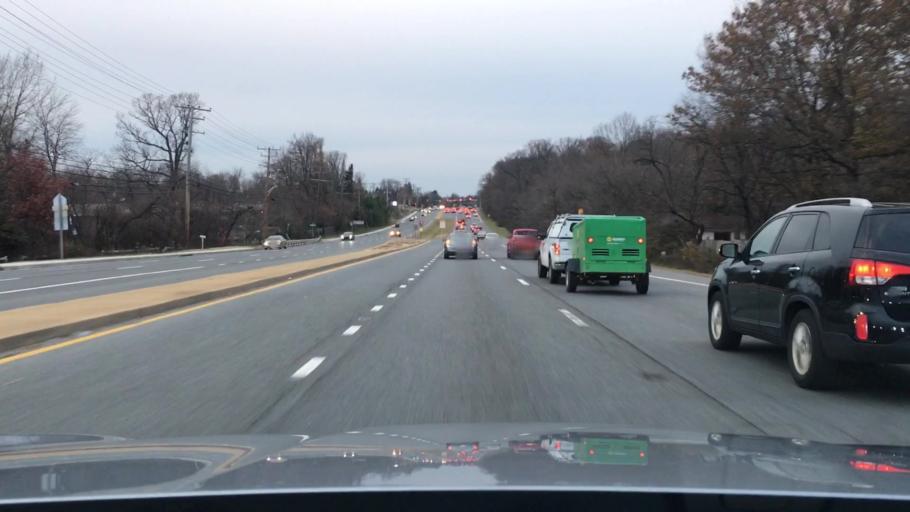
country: US
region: Maryland
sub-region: Prince George's County
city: South Laurel
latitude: 39.0807
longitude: -76.8479
